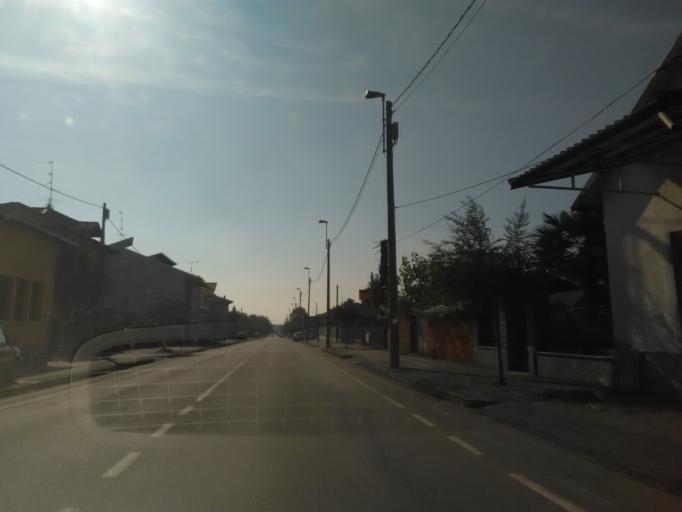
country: IT
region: Piedmont
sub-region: Provincia di Vercelli
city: Gattinara
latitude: 45.6054
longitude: 8.3716
